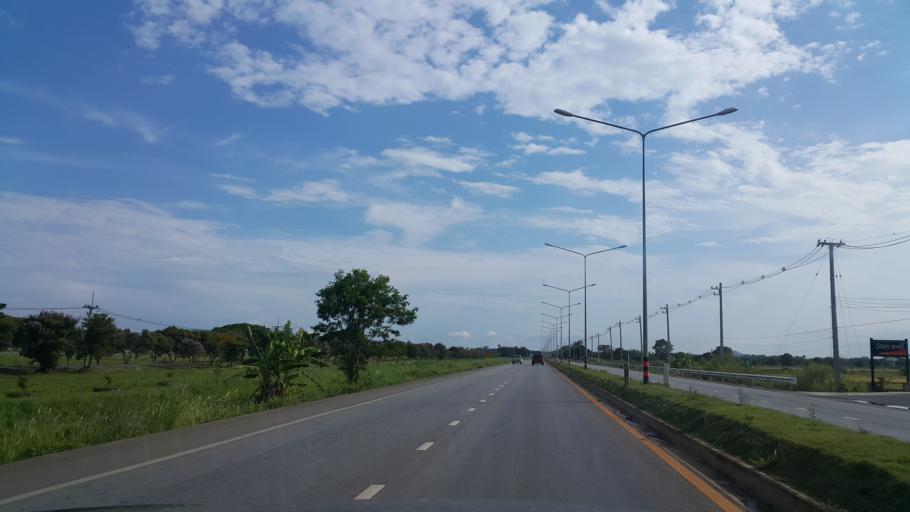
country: TH
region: Chiang Rai
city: Chiang Rai
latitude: 19.9432
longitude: 99.8702
